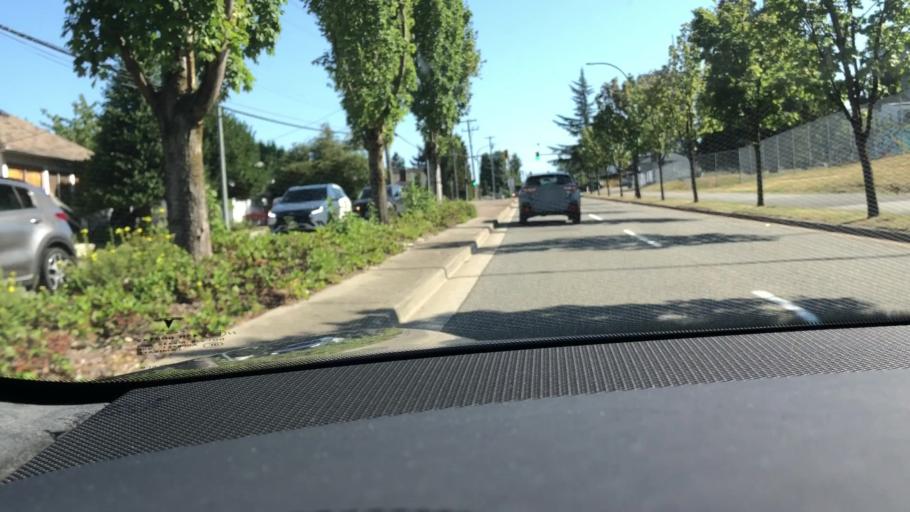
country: CA
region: British Columbia
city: Burnaby
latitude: 49.2290
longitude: -122.9891
